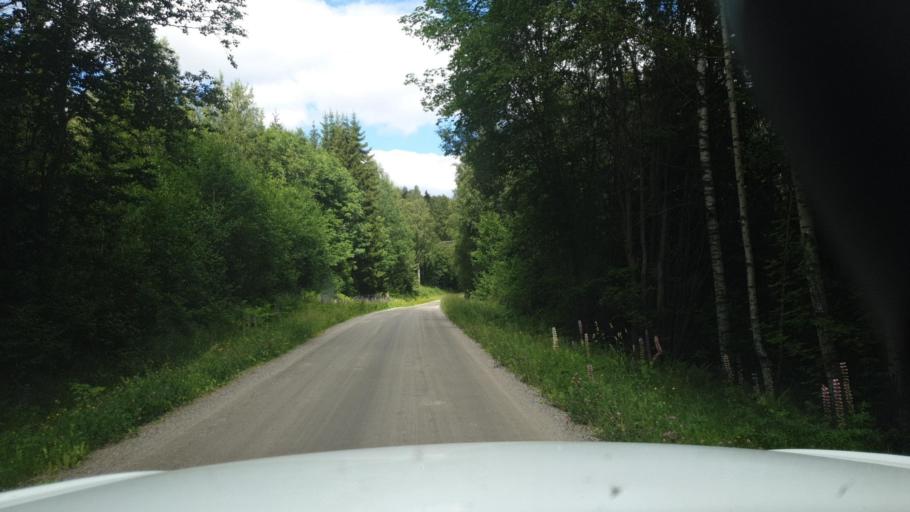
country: SE
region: Vaermland
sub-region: Eda Kommun
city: Amotfors
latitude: 59.7366
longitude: 12.2788
